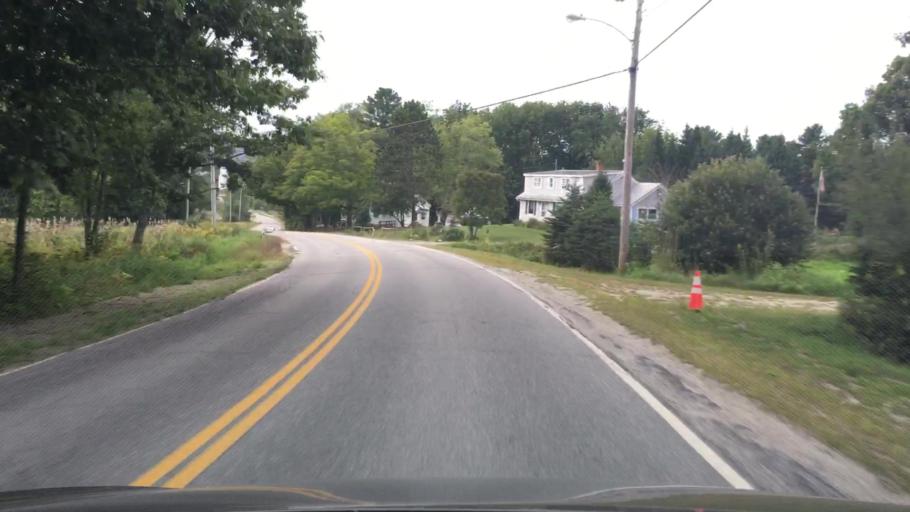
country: US
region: Maine
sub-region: Hancock County
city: Penobscot
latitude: 44.4606
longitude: -68.7058
